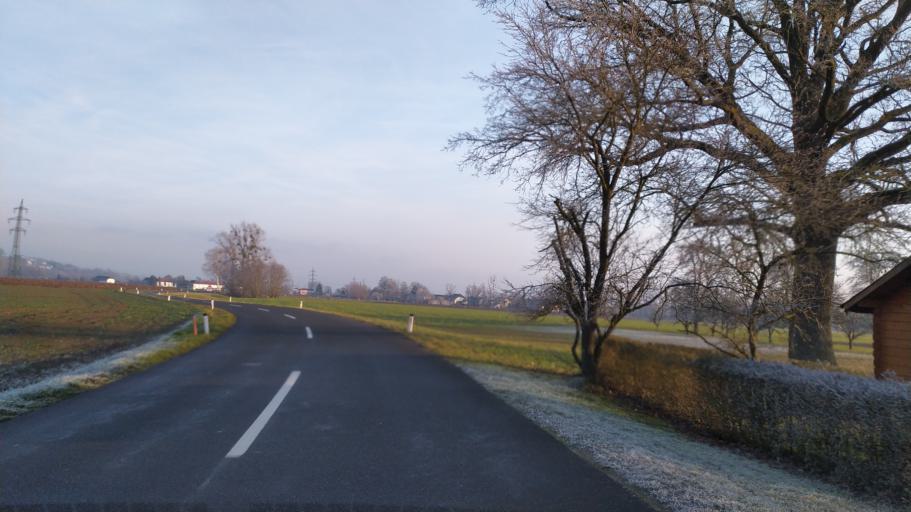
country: AT
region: Upper Austria
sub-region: Politischer Bezirk Urfahr-Umgebung
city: Goldworth
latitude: 48.3398
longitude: 14.0877
